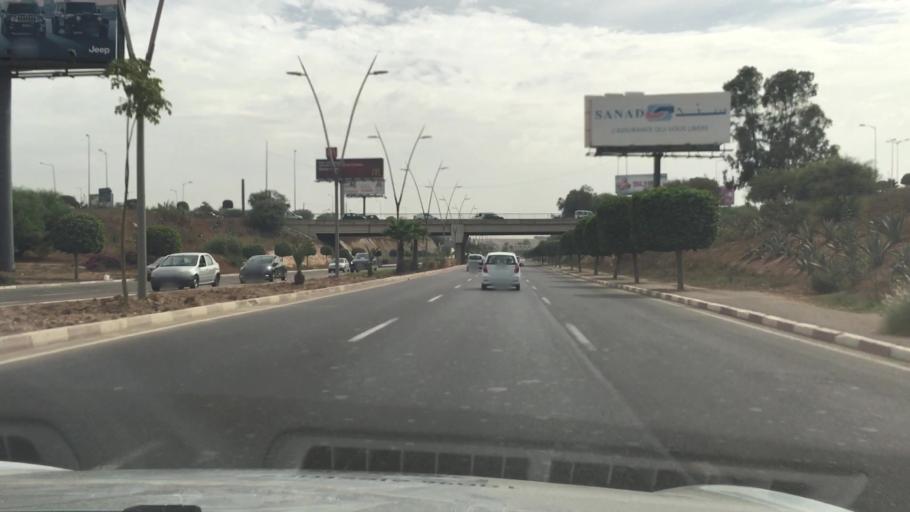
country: MA
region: Grand Casablanca
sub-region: Casablanca
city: Casablanca
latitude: 33.5202
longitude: -7.6336
